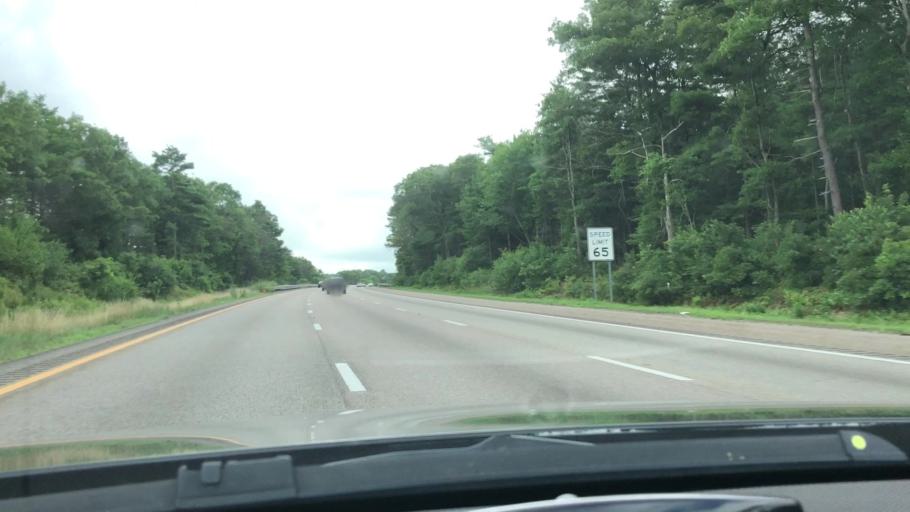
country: US
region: Massachusetts
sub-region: Norfolk County
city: Foxborough
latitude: 42.0878
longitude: -71.2225
